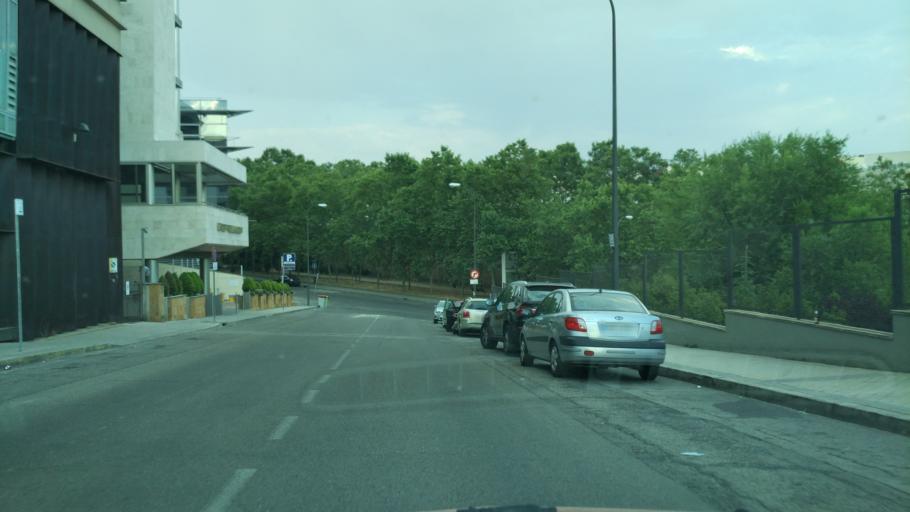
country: ES
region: Madrid
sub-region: Provincia de Madrid
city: Pinar de Chamartin
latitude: 40.4895
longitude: -3.6886
